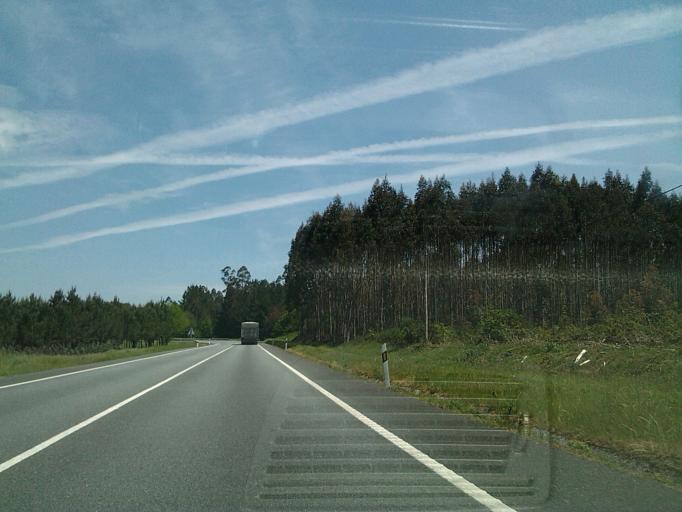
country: ES
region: Galicia
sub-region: Provincia da Coruna
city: Frades
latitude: 42.9698
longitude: -8.2986
